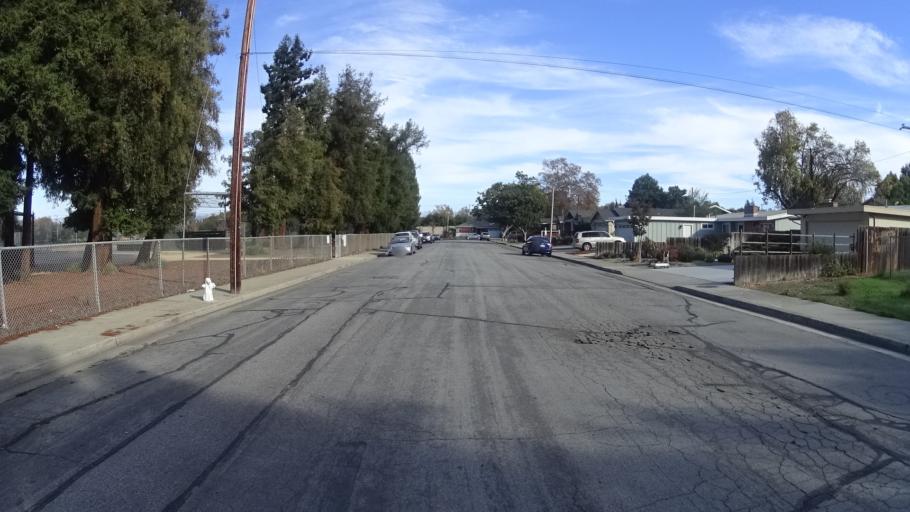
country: US
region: California
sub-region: Santa Clara County
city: Santa Clara
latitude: 37.3565
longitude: -121.9707
